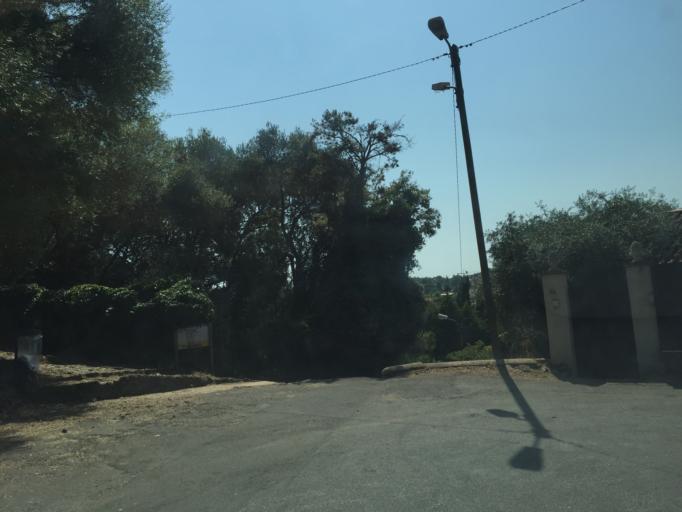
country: FR
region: Provence-Alpes-Cote d'Azur
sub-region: Departement des Alpes-Maritimes
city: Antibes
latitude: 43.5690
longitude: 7.1330
